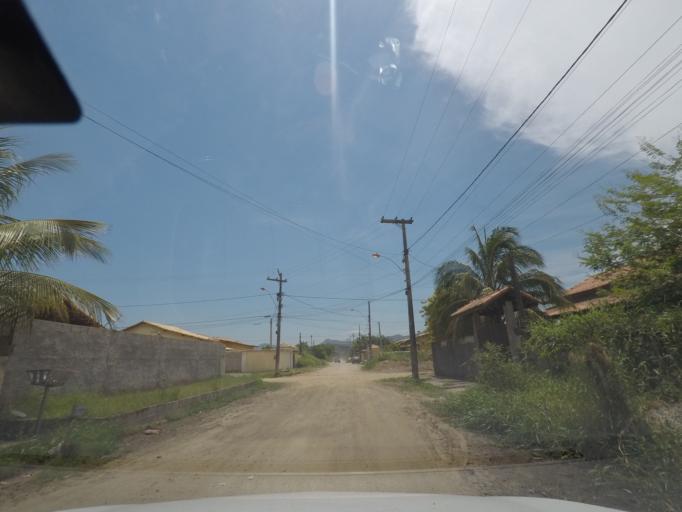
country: BR
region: Rio de Janeiro
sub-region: Marica
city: Marica
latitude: -22.9543
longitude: -42.9511
